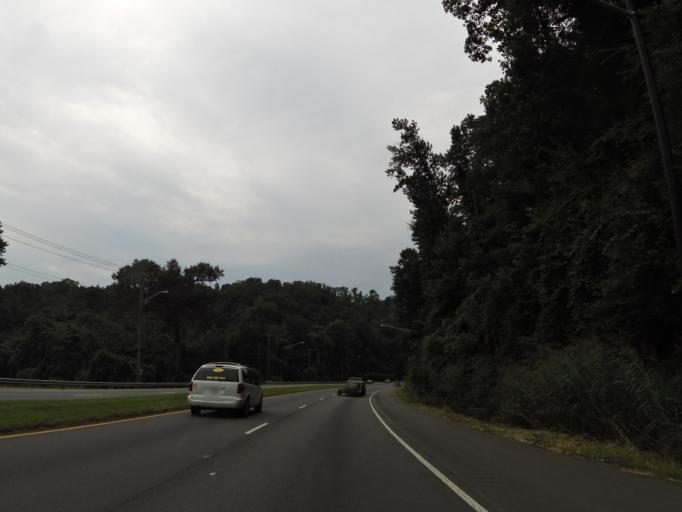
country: US
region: Tennessee
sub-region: Knox County
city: Knoxville
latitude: 35.9197
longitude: -83.9565
